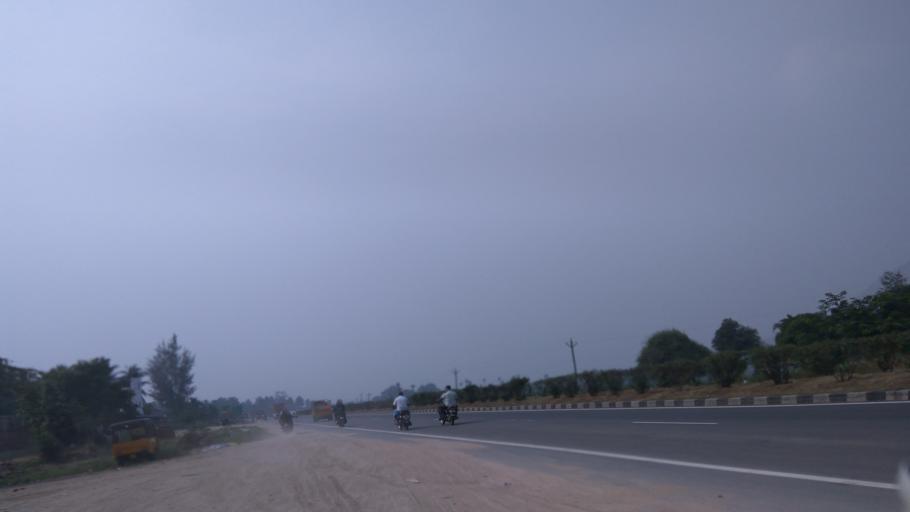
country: IN
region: Tamil Nadu
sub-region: Krishnagiri
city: Krishnagiri
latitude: 12.4885
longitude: 78.2186
